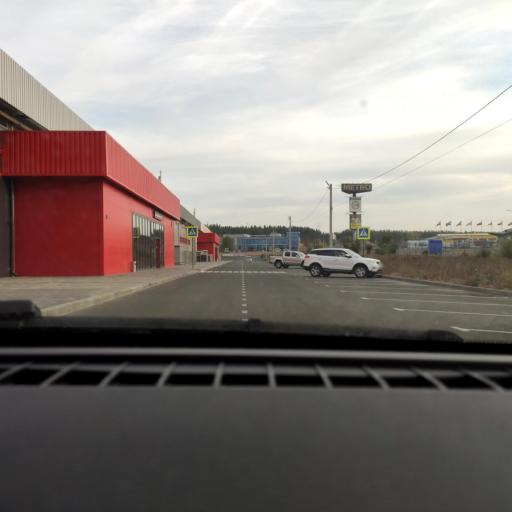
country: RU
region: Voronezj
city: Voronezh
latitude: 51.6785
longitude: 39.2823
